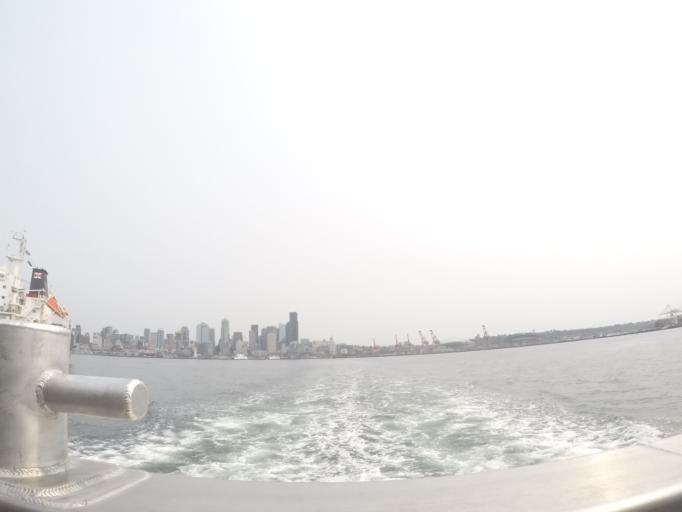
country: US
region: Washington
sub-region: King County
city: Seattle
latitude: 47.5958
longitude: -122.3650
